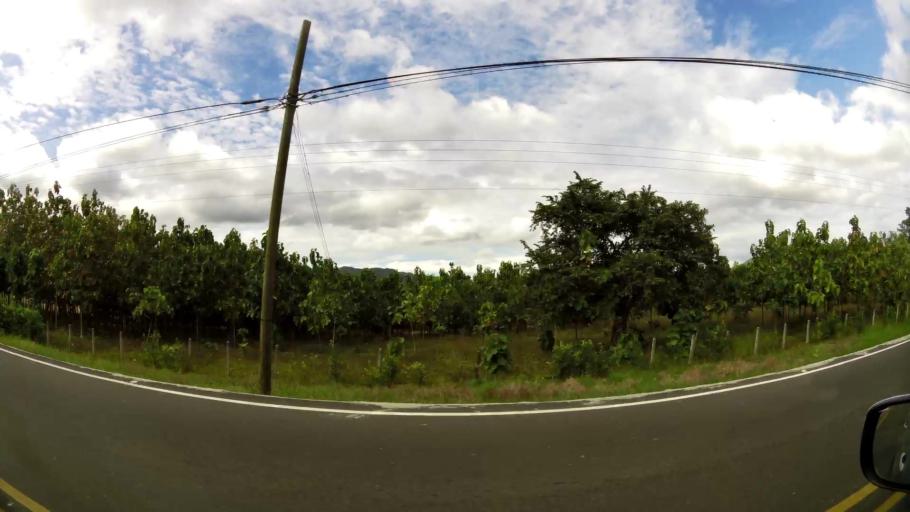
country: CR
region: Guanacaste
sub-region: Canton de Nicoya
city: Nicoya
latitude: 10.1406
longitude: -85.3344
